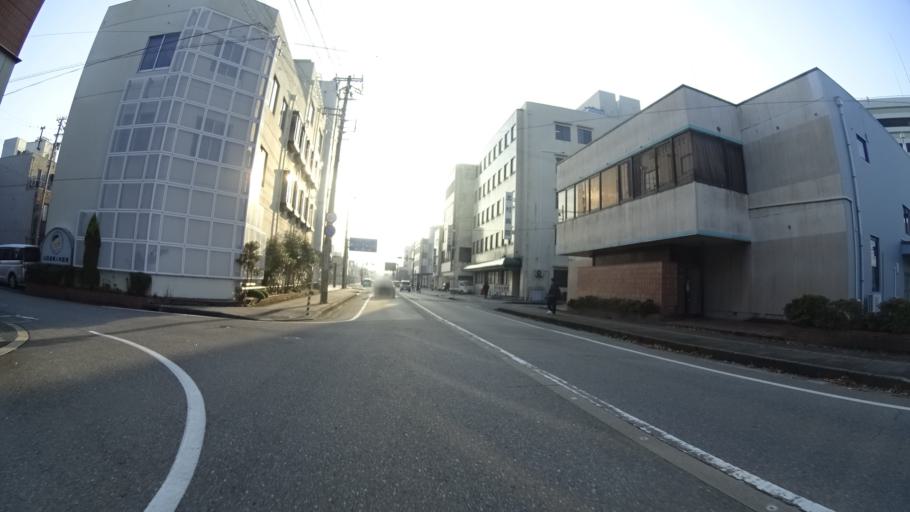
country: JP
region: Ishikawa
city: Nanao
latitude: 37.0443
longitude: 136.9630
